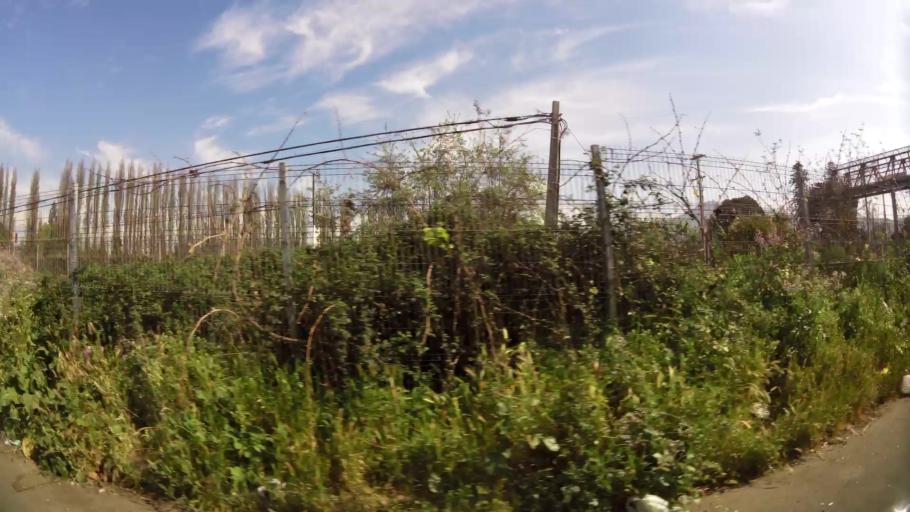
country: CL
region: Santiago Metropolitan
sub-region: Provincia de Talagante
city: El Monte
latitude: -33.6788
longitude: -70.9561
